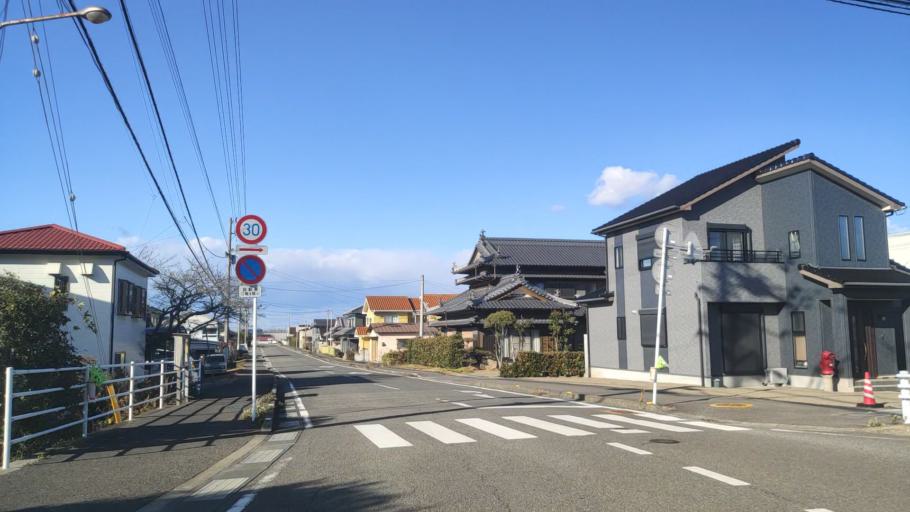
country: JP
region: Ehime
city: Saijo
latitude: 33.9286
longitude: 133.1655
